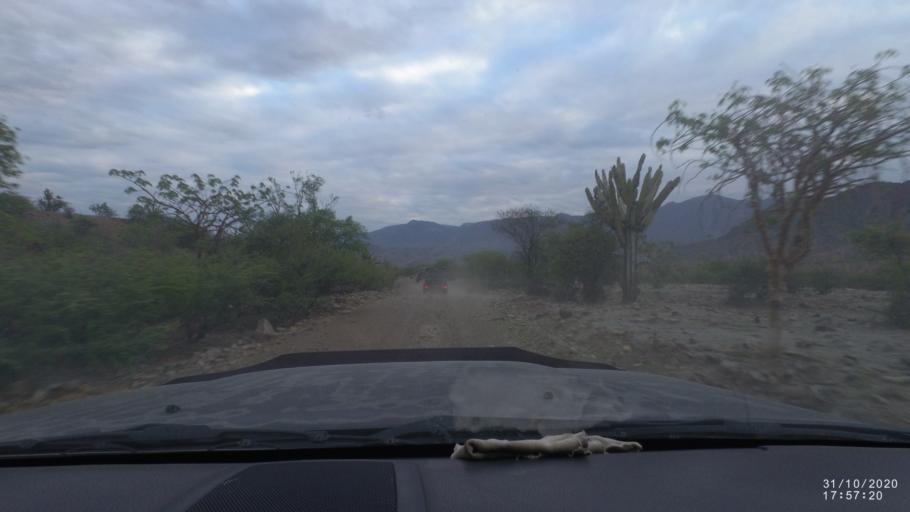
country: BO
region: Chuquisaca
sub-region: Provincia Zudanez
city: Mojocoya
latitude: -18.6502
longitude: -64.5319
